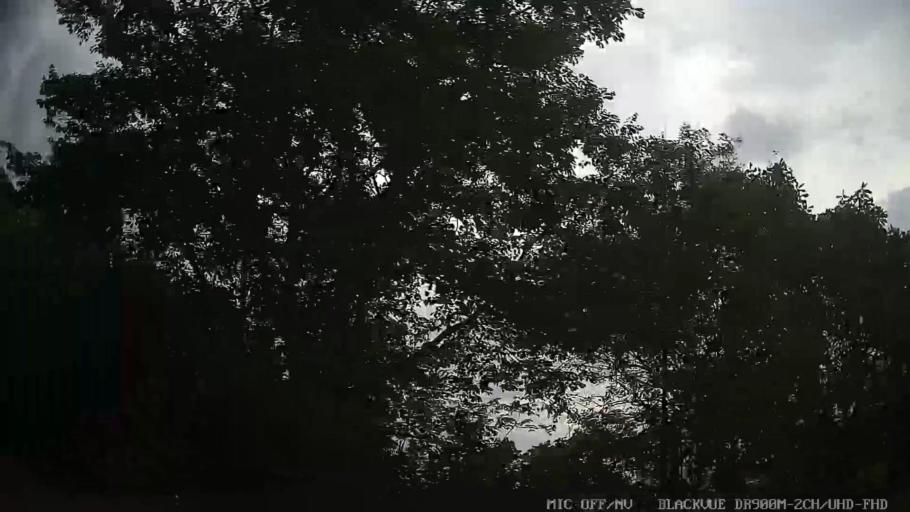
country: BR
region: Sao Paulo
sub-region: Amparo
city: Amparo
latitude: -22.6973
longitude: -46.7599
